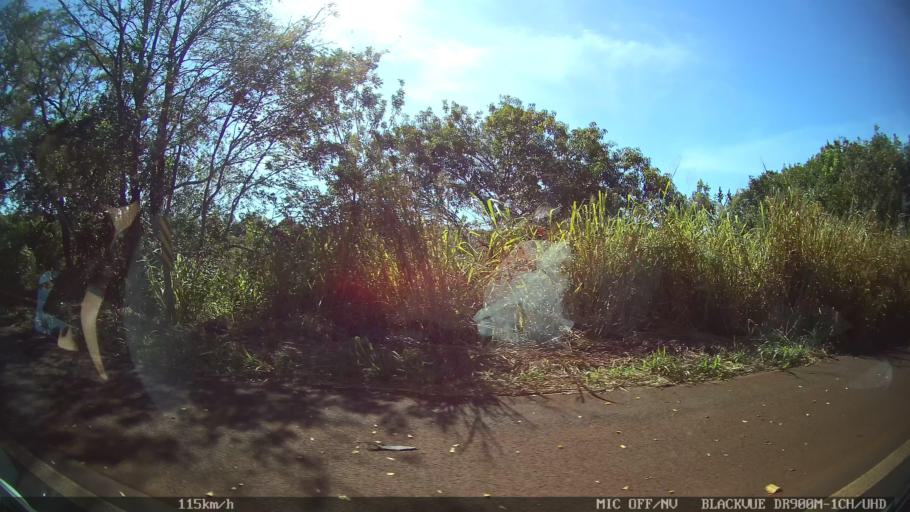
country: BR
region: Sao Paulo
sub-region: Guaira
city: Guaira
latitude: -20.4434
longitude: -48.3271
